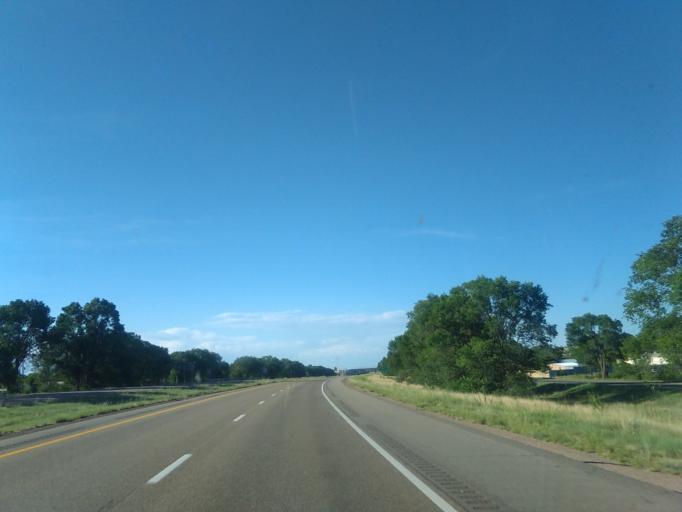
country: US
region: New Mexico
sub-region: San Miguel County
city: Las Vegas
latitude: 35.5843
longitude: -105.2119
